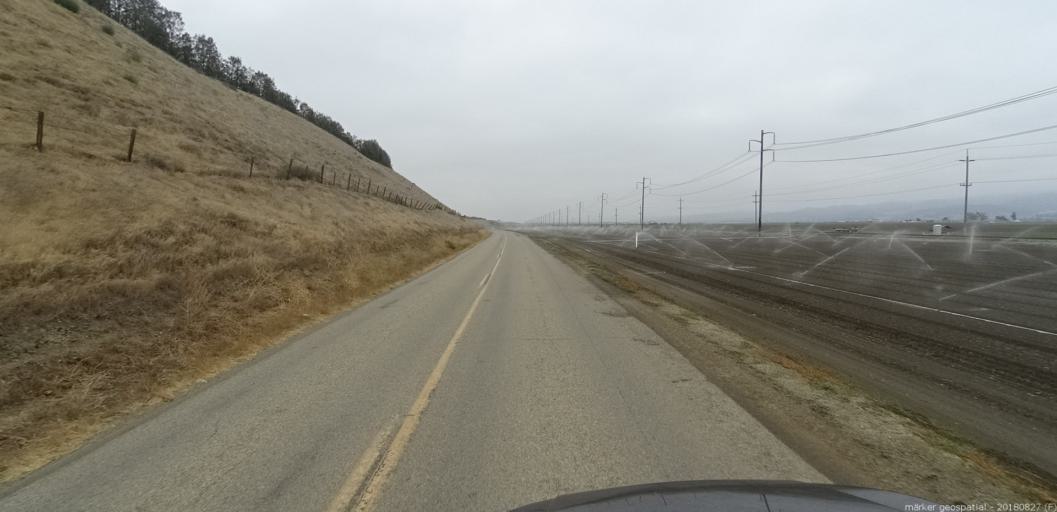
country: US
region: California
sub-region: Monterey County
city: King City
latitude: 36.2626
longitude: -121.1425
